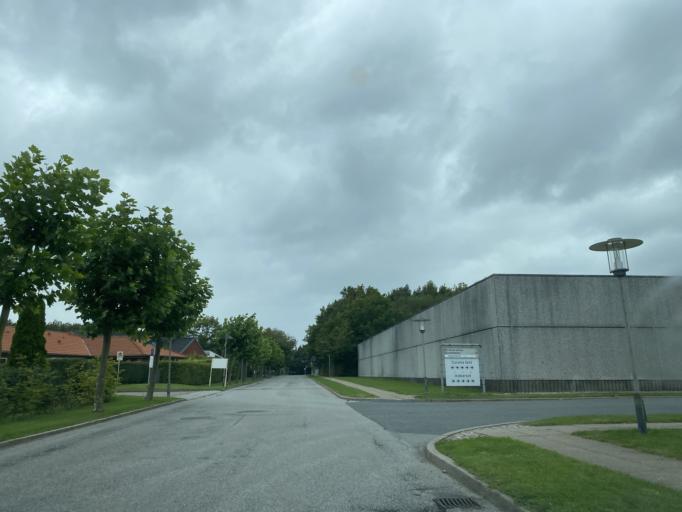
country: DK
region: South Denmark
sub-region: Sonderborg Kommune
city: Sonderborg
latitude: 54.9197
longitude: 9.7817
